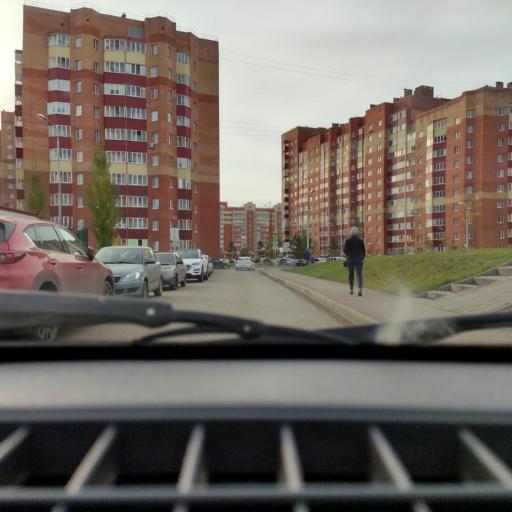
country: RU
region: Bashkortostan
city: Mikhaylovka
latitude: 54.7146
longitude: 55.8412
